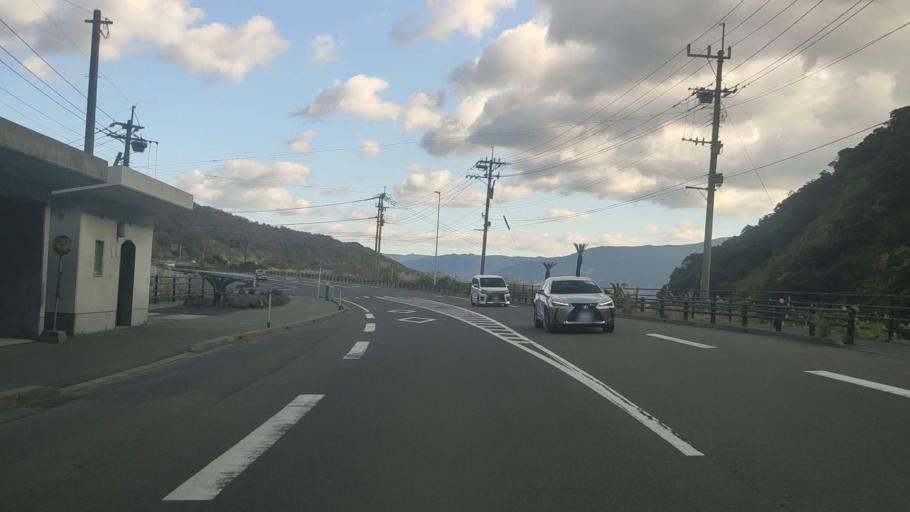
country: JP
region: Kagoshima
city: Tarumizu
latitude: 31.5570
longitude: 130.7034
